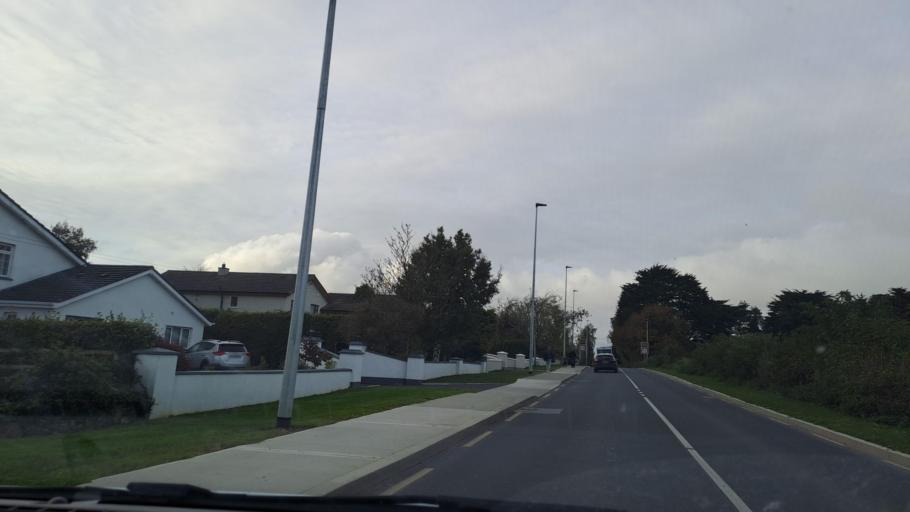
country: IE
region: Leinster
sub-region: An Mhi
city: Navan
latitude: 53.7071
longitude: -6.6863
